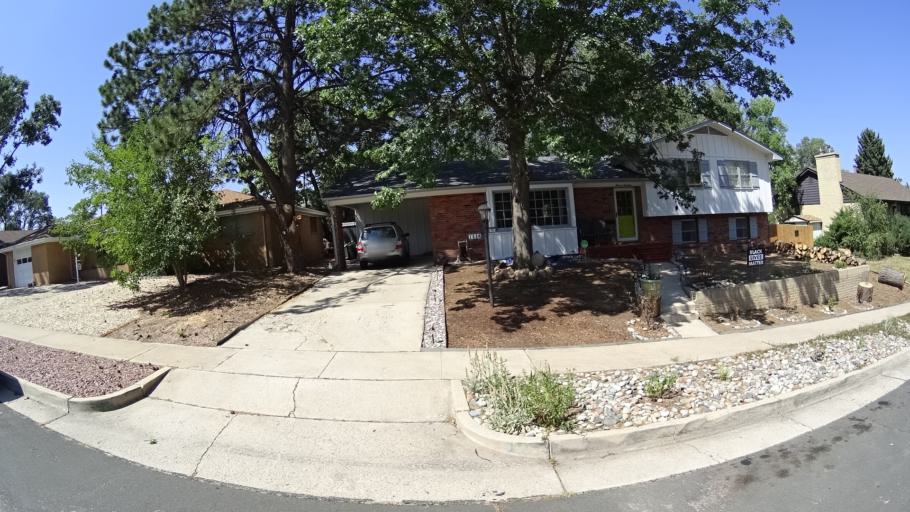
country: US
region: Colorado
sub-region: El Paso County
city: Colorado Springs
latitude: 38.8490
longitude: -104.7989
